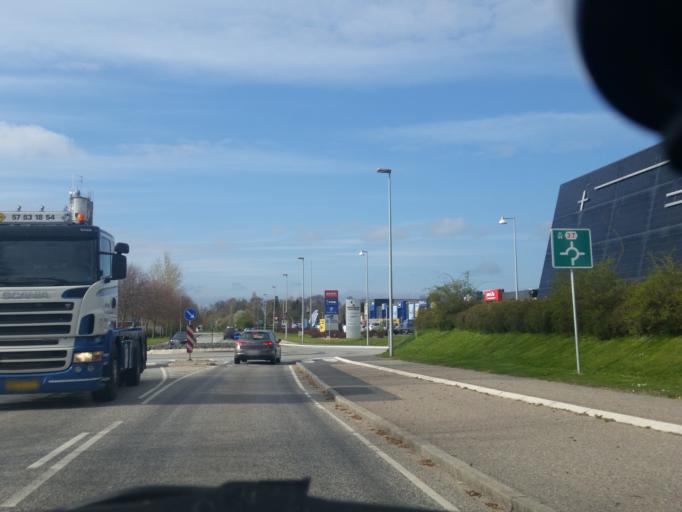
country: DK
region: Zealand
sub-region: Soro Kommune
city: Soro
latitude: 55.4433
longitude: 11.5653
